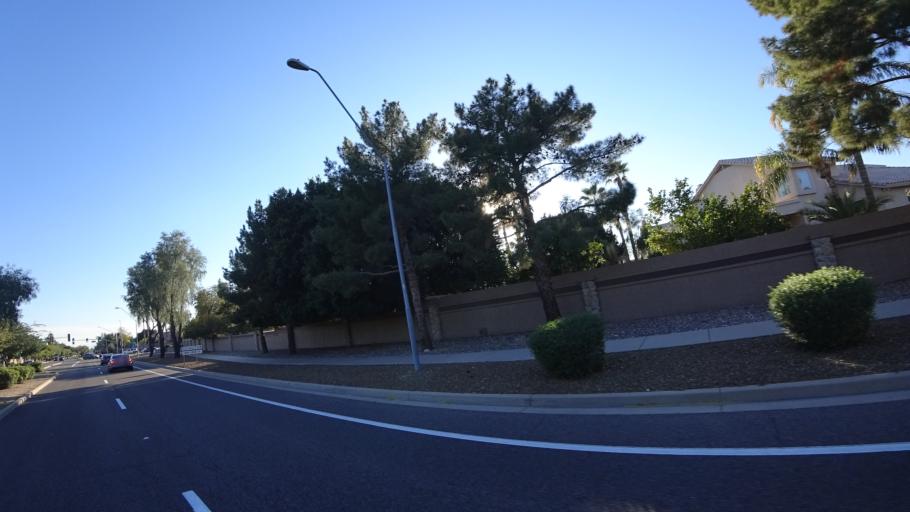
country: US
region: Arizona
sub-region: Maricopa County
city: Peoria
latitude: 33.6843
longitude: -112.1867
